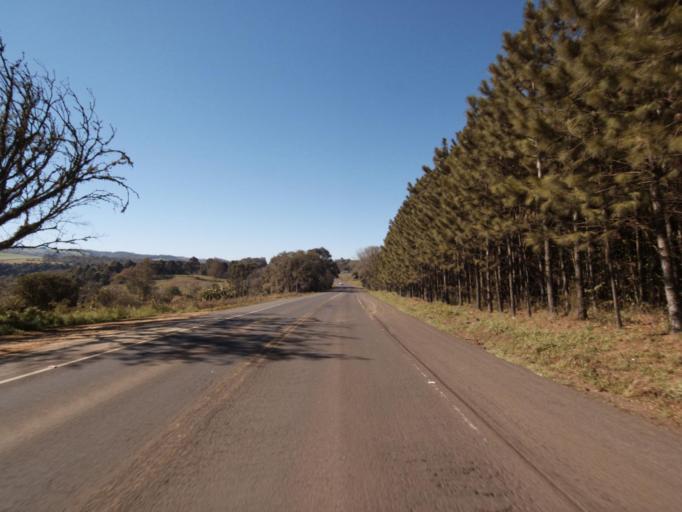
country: BR
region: Santa Catarina
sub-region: Sao Lourenco Do Oeste
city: Sao Lourenco dOeste
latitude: -26.8294
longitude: -53.1282
